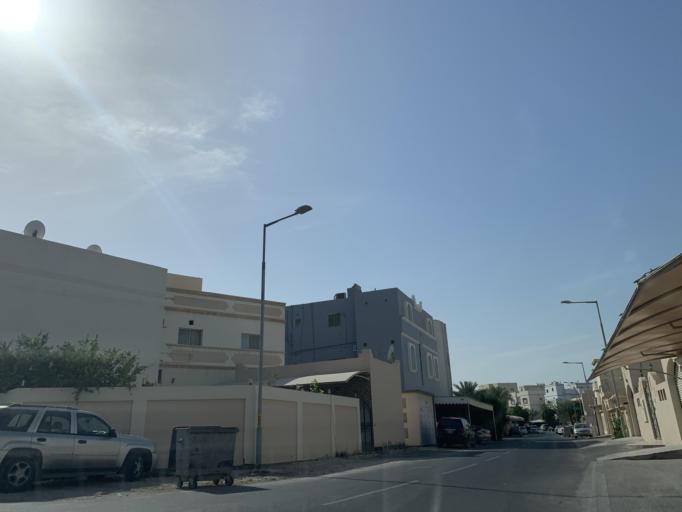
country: BH
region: Northern
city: Ar Rifa'
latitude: 26.1270
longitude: 50.5827
